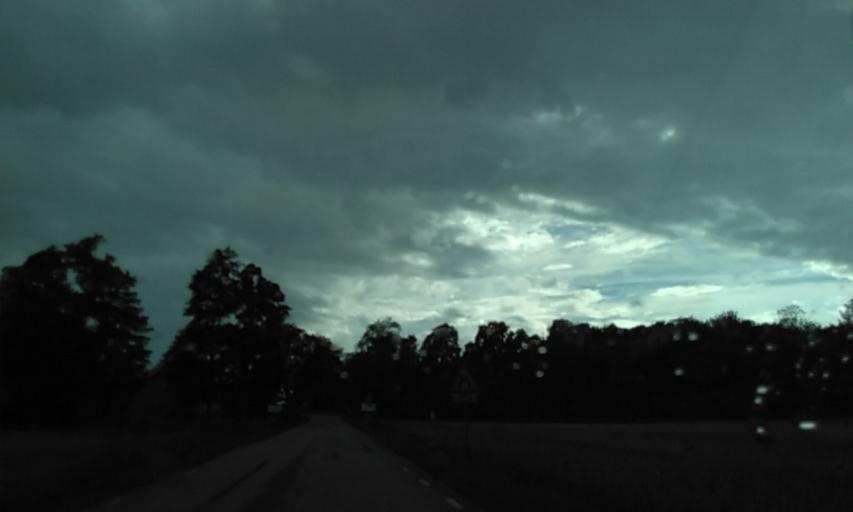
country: SE
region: Vaestra Goetaland
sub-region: Grastorps Kommun
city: Graestorp
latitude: 58.4323
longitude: 12.7402
